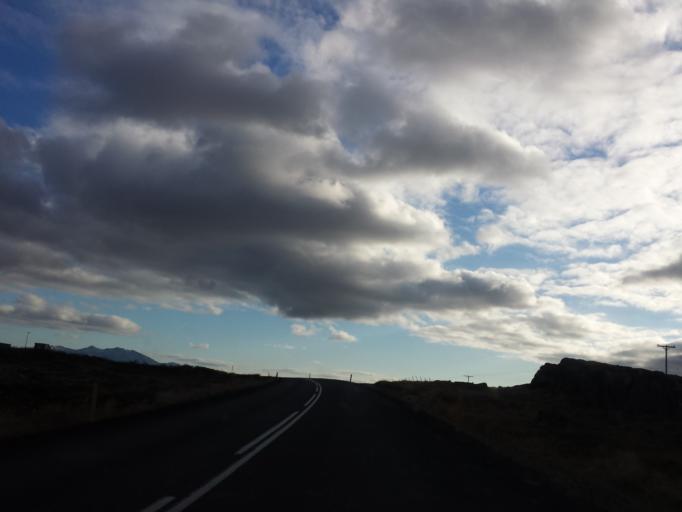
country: IS
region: West
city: Borgarnes
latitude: 64.6311
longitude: -22.0674
